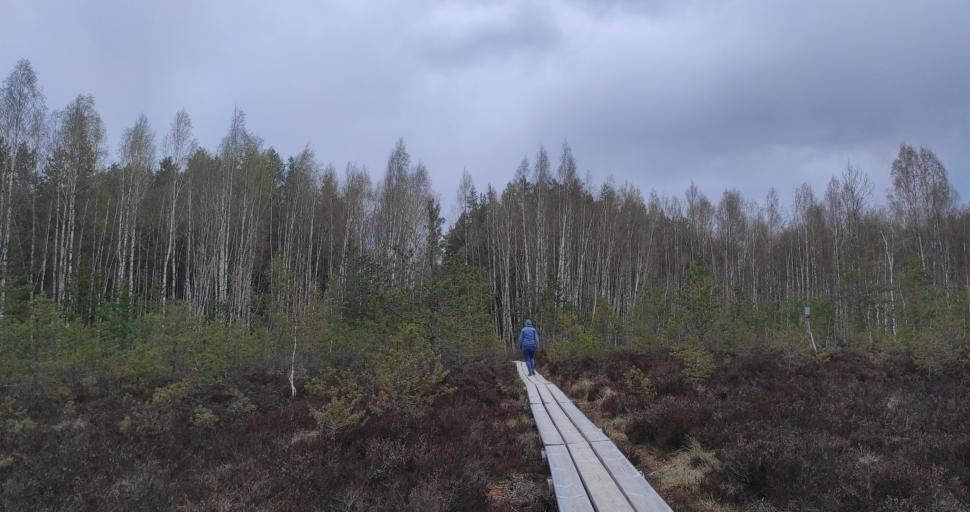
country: LV
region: Dundaga
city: Dundaga
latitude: 57.3559
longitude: 22.1539
